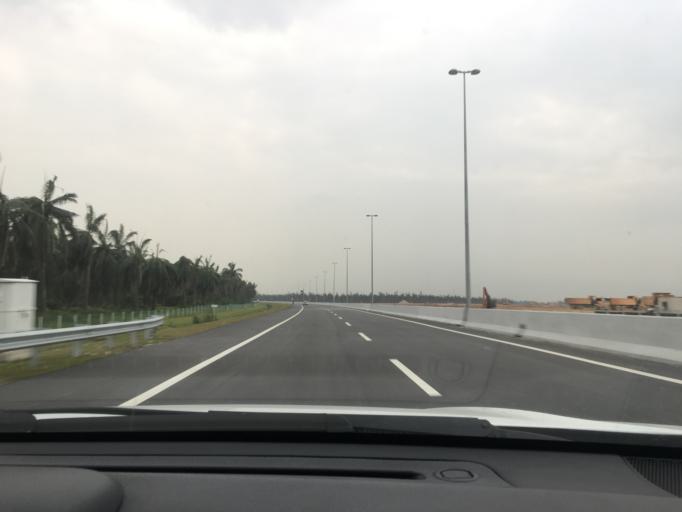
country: MY
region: Selangor
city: Klang
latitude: 3.1102
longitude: 101.4139
